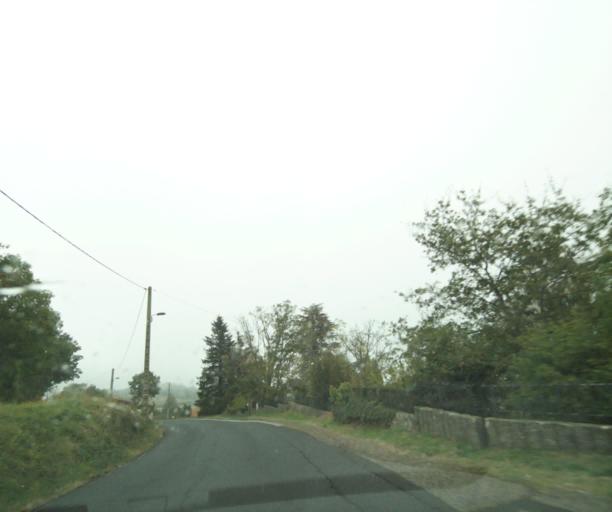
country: FR
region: Auvergne
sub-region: Departement du Puy-de-Dome
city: Ceyrat
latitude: 45.7251
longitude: 3.0483
